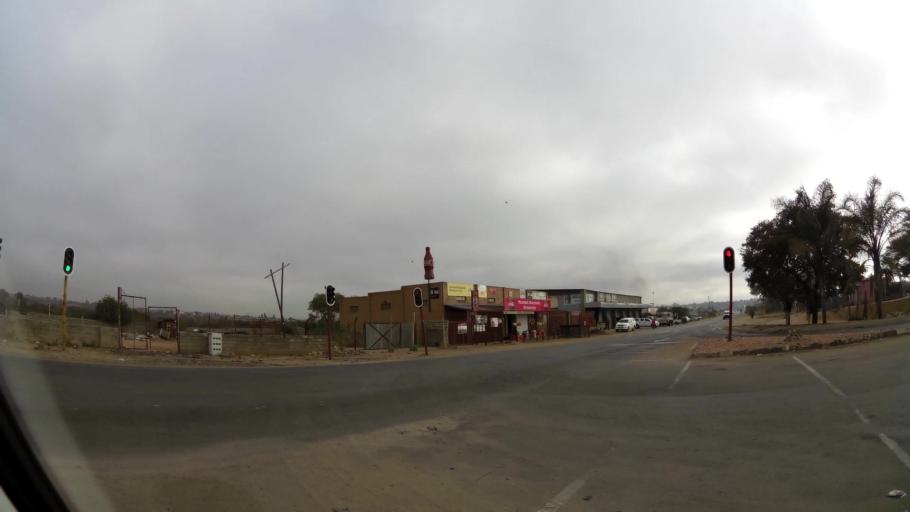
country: ZA
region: Limpopo
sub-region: Capricorn District Municipality
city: Polokwane
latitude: -23.8340
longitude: 29.3794
